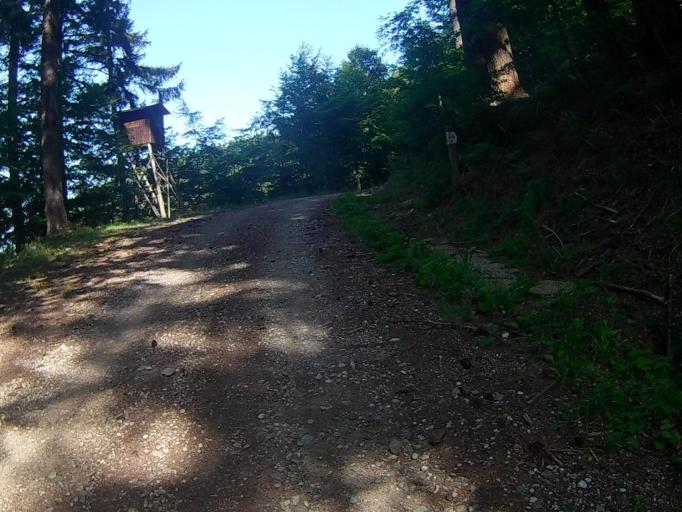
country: SI
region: Ruse
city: Bistrica ob Dravi
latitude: 46.5121
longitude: 15.5489
